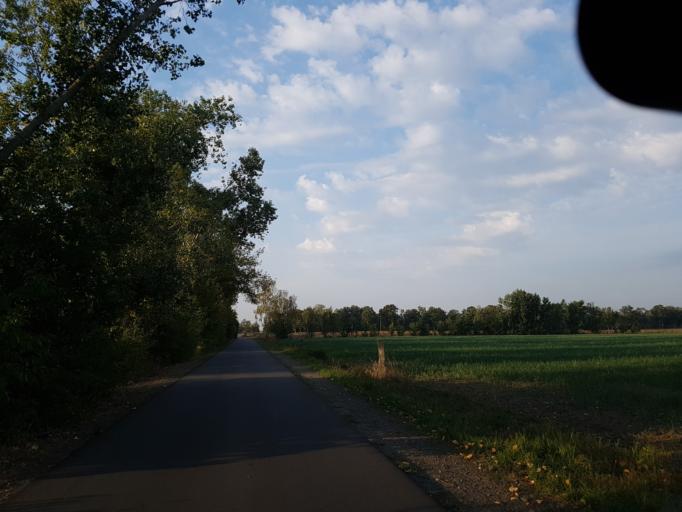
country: DE
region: Brandenburg
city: Elsterwerda
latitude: 51.4576
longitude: 13.5582
